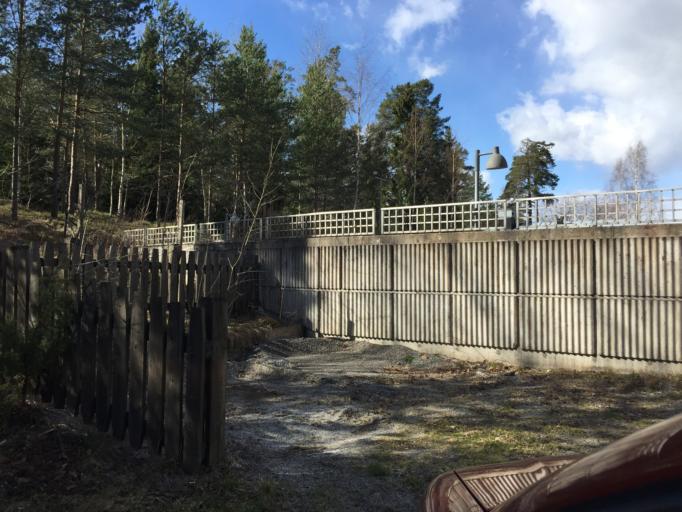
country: SE
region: Stockholm
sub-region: Salems Kommun
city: Ronninge
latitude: 59.2104
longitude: 17.7580
